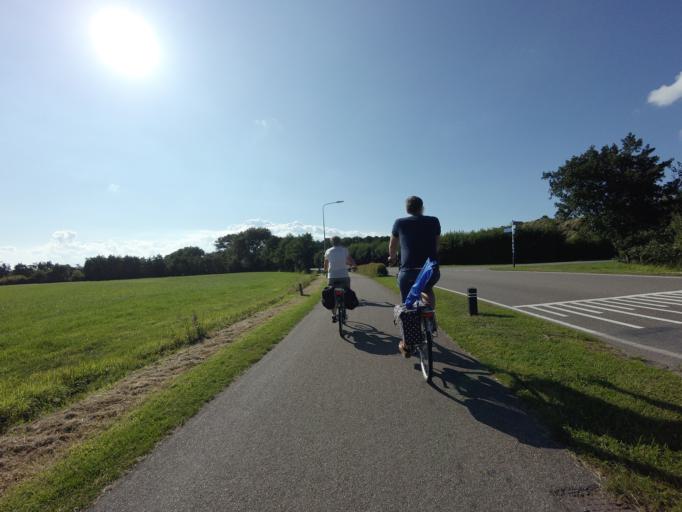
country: NL
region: Friesland
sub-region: Gemeente Terschelling
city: West-Terschelling
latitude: 53.3738
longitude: 5.2441
